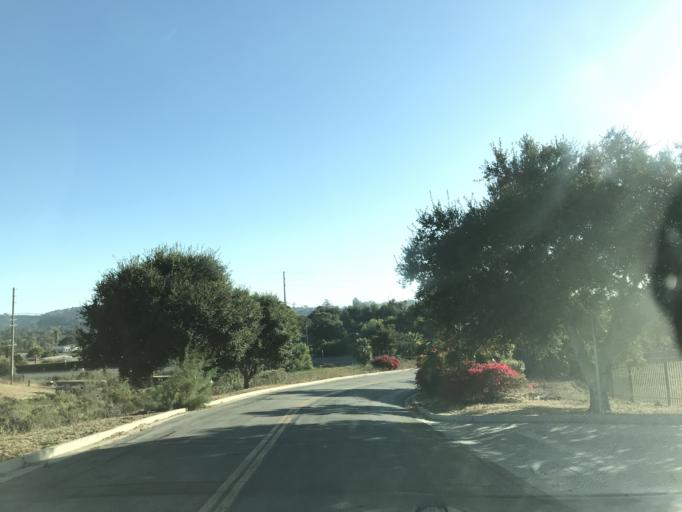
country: US
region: California
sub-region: Santa Barbara County
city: Mission Canyon
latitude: 34.4506
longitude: -119.7687
